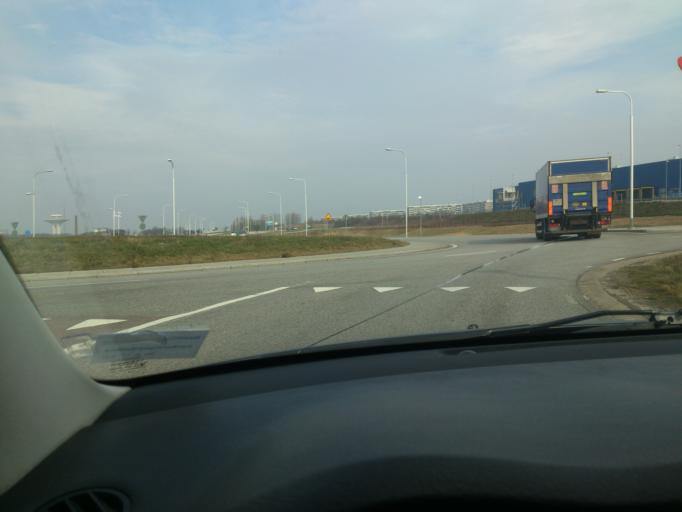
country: SE
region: Skane
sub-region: Malmo
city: Bunkeflostrand
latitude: 55.5507
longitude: 12.9829
